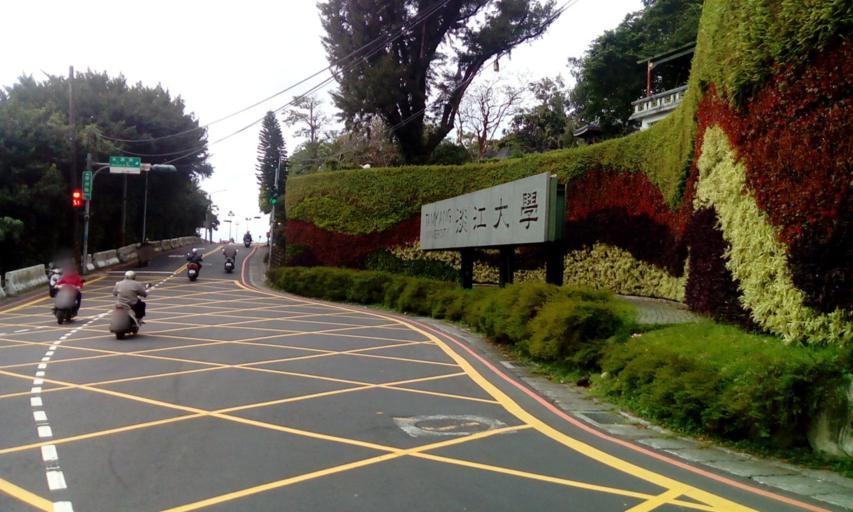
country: TW
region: Taipei
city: Taipei
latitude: 25.1734
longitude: 121.4486
